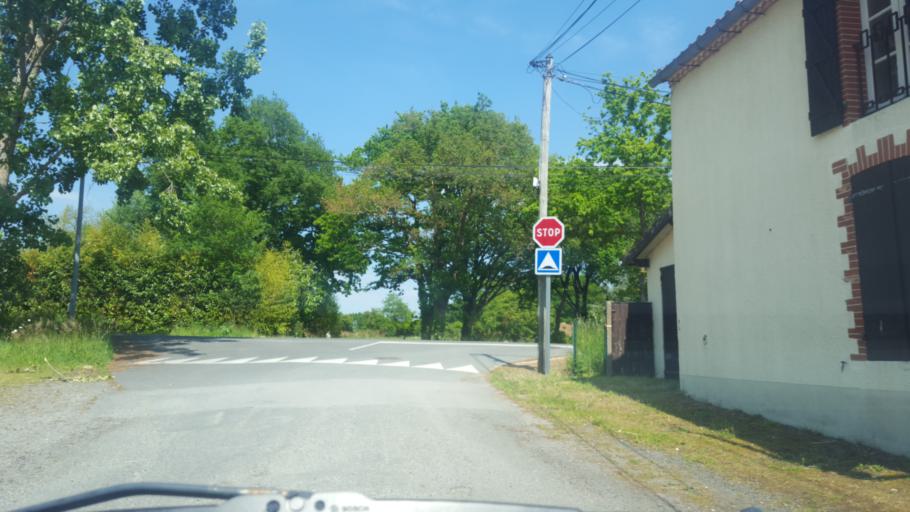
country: FR
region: Pays de la Loire
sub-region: Departement de la Loire-Atlantique
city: La Limouziniere
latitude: 47.0211
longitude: -1.5693
